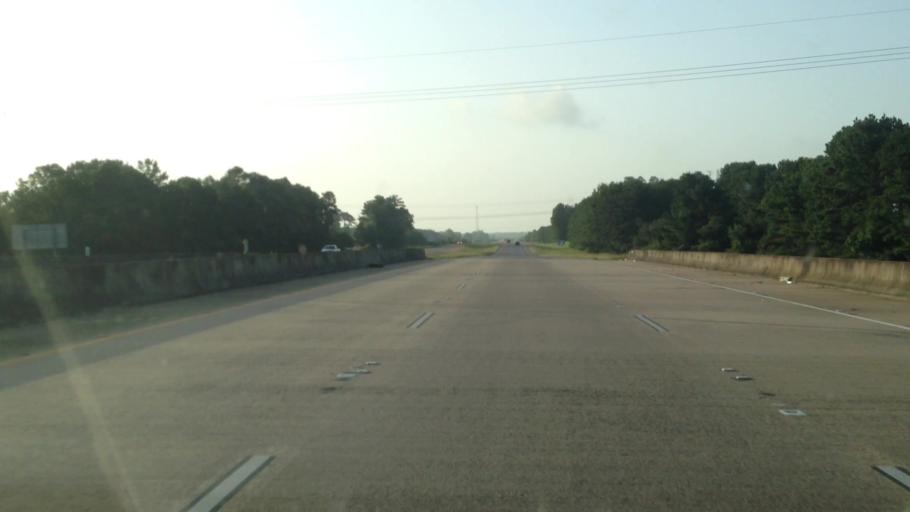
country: US
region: Louisiana
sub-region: Rapides Parish
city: Boyce
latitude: 31.4053
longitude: -92.7112
